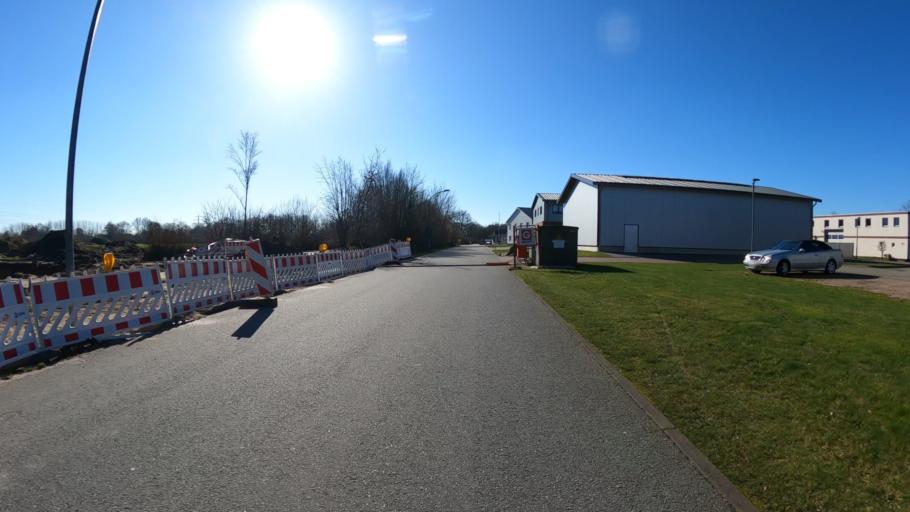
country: DE
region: Schleswig-Holstein
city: Kummerfeld
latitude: 53.6857
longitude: 9.7824
